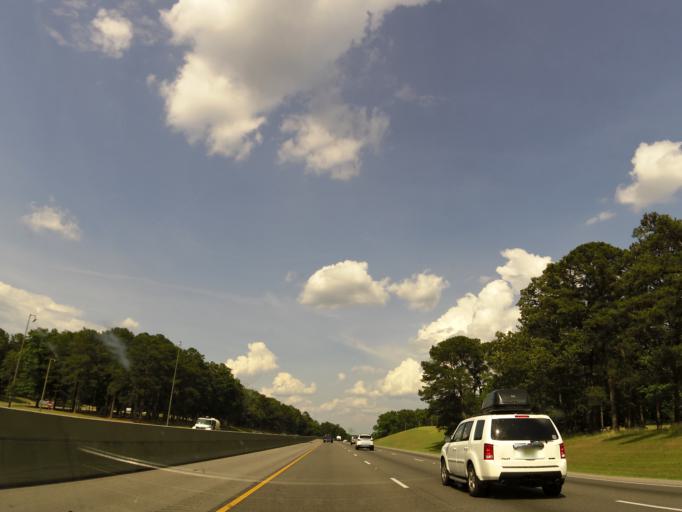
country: US
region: Alabama
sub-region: Tuscaloosa County
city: Coaling
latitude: 33.1887
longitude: -87.3275
